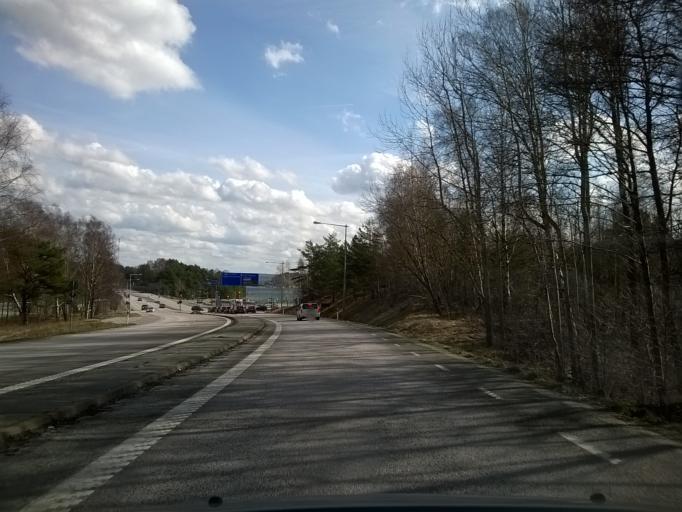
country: SE
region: Vaestra Goetaland
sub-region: Tjorns Kommun
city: Myggenas
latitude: 58.0581
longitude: 11.7575
